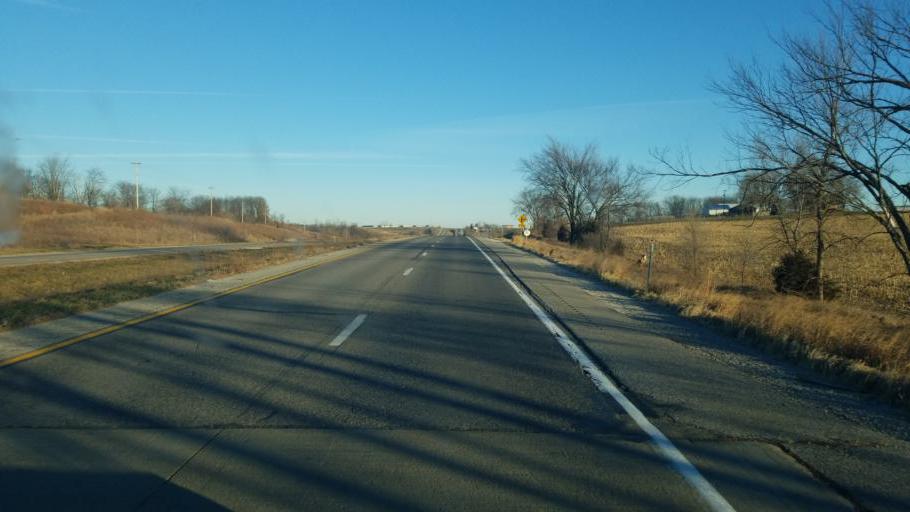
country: US
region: Iowa
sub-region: Wapello County
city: Eddyville
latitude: 41.2160
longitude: -92.6404
